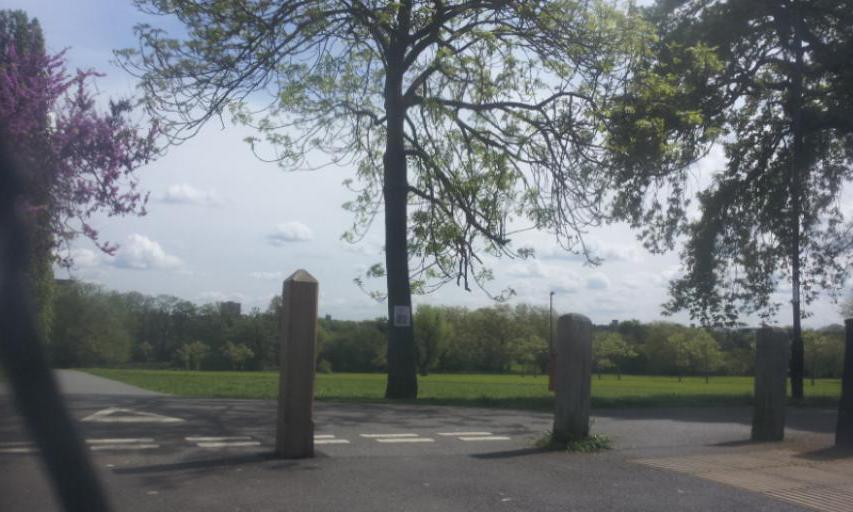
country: GB
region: England
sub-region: Greater London
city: Catford
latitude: 51.4494
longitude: -0.0288
